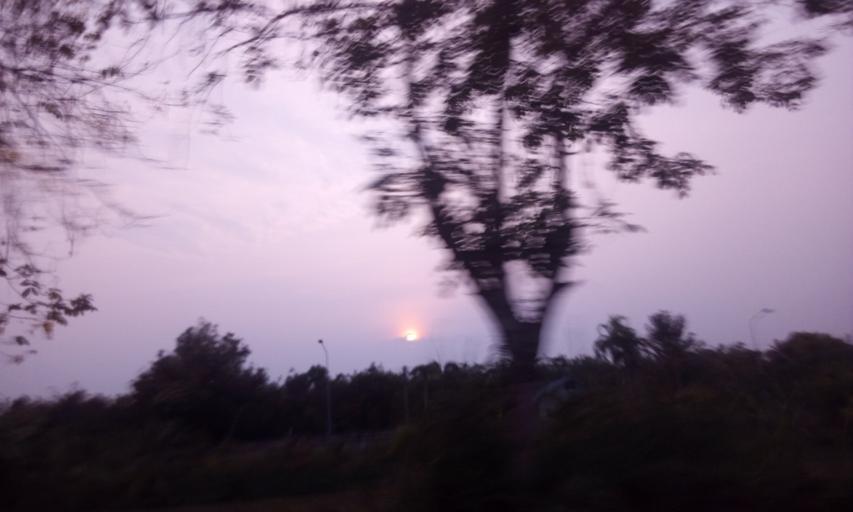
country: TH
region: Pathum Thani
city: Ban Lam Luk Ka
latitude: 13.9906
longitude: 100.8952
